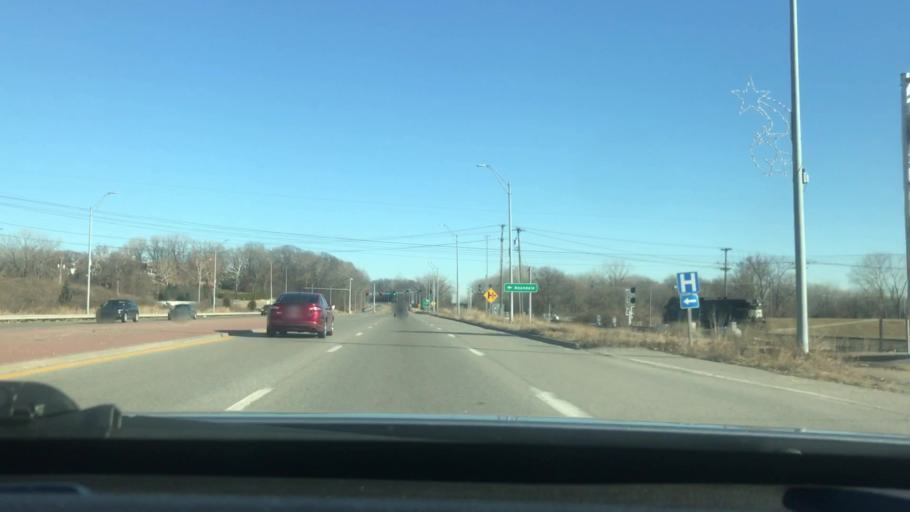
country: US
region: Missouri
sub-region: Clay County
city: North Kansas City
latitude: 39.1460
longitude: -94.5501
